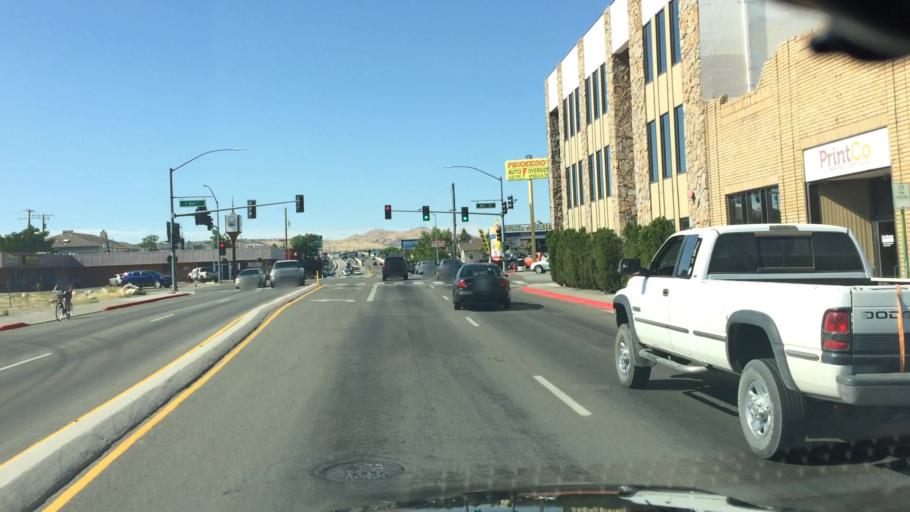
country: US
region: Nevada
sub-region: Washoe County
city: Reno
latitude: 39.5251
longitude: -119.8030
